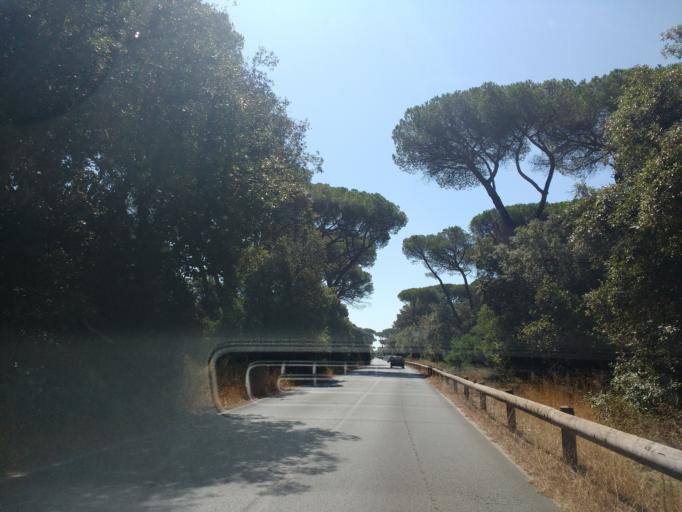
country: IT
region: Latium
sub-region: Citta metropolitana di Roma Capitale
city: Acilia-Castel Fusano-Ostia Antica
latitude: 41.7236
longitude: 12.3442
